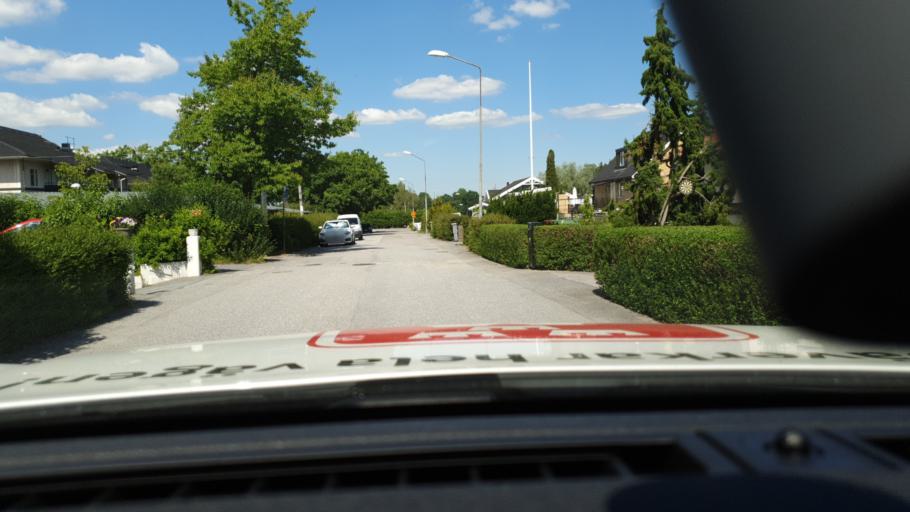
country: SE
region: Stockholm
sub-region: Vallentuna Kommun
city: Vallentuna
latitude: 59.5173
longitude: 18.0647
